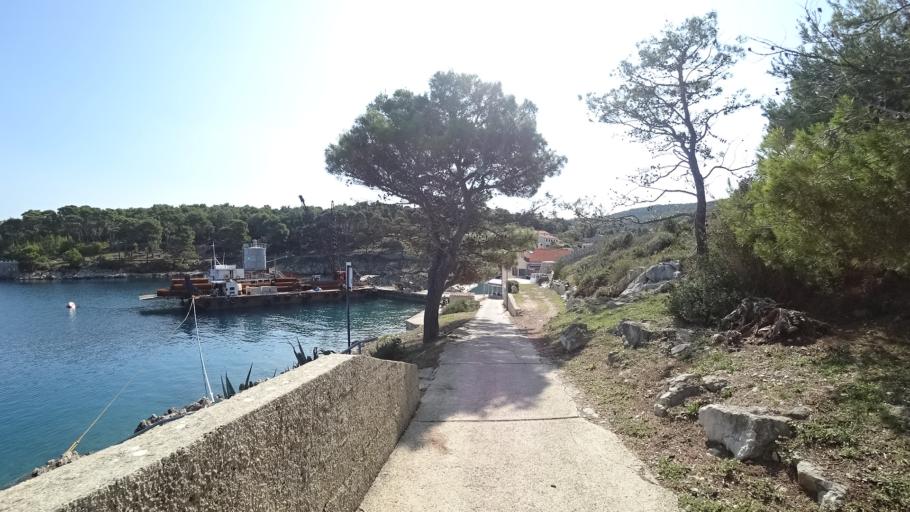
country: HR
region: Primorsko-Goranska
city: Mali Losinj
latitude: 44.5208
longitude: 14.5056
